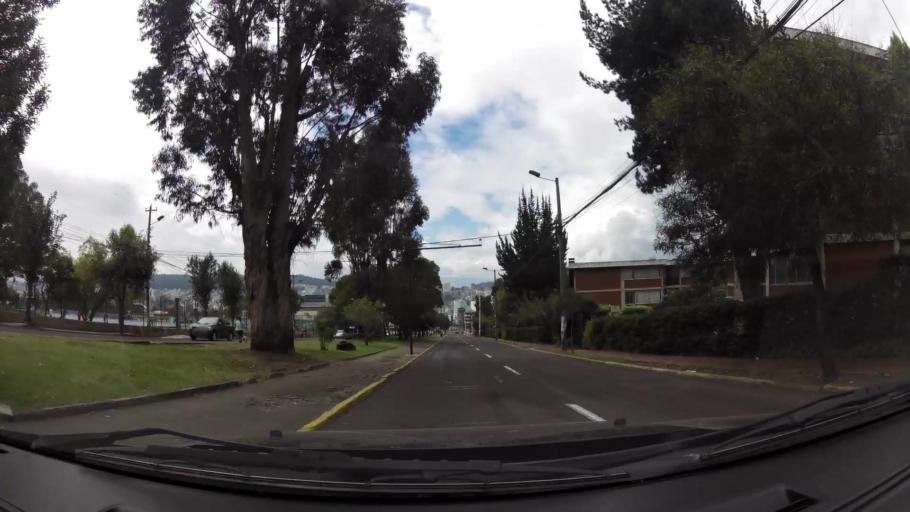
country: EC
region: Pichincha
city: Quito
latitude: -0.1854
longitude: -78.4984
